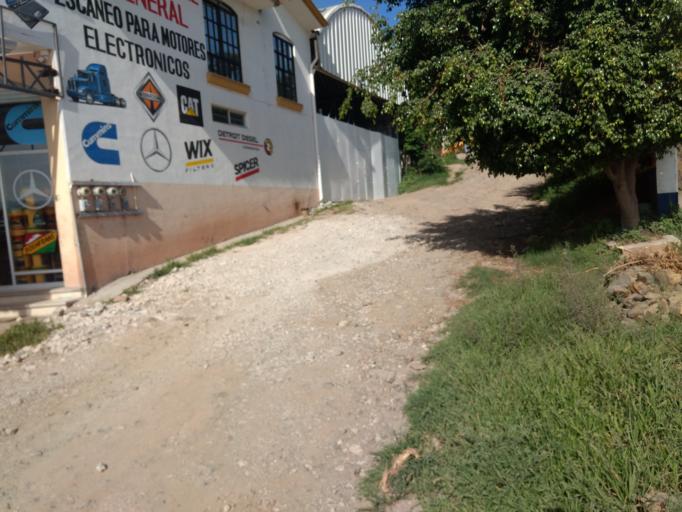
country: MX
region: Oaxaca
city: Ciudad de Huajuapam de Leon
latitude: 17.8164
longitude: -97.7904
